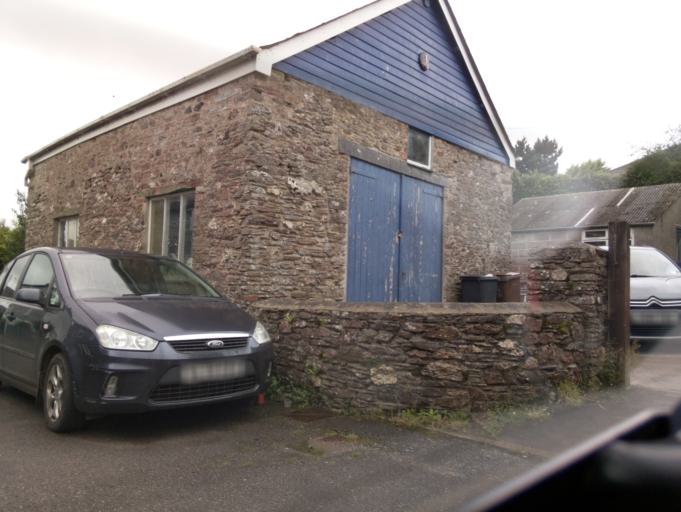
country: GB
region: England
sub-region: Devon
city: Totnes
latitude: 50.3452
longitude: -3.6815
